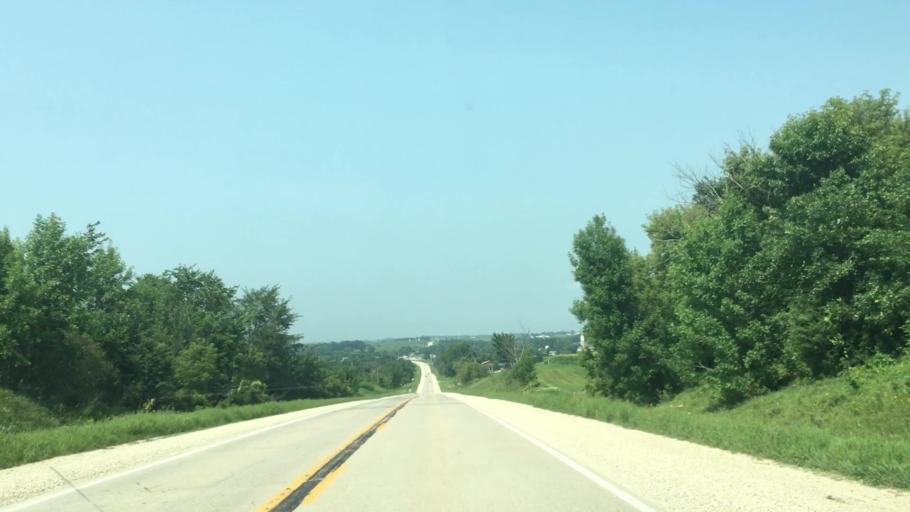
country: US
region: Iowa
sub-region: Fayette County
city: West Union
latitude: 43.1041
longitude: -91.8691
